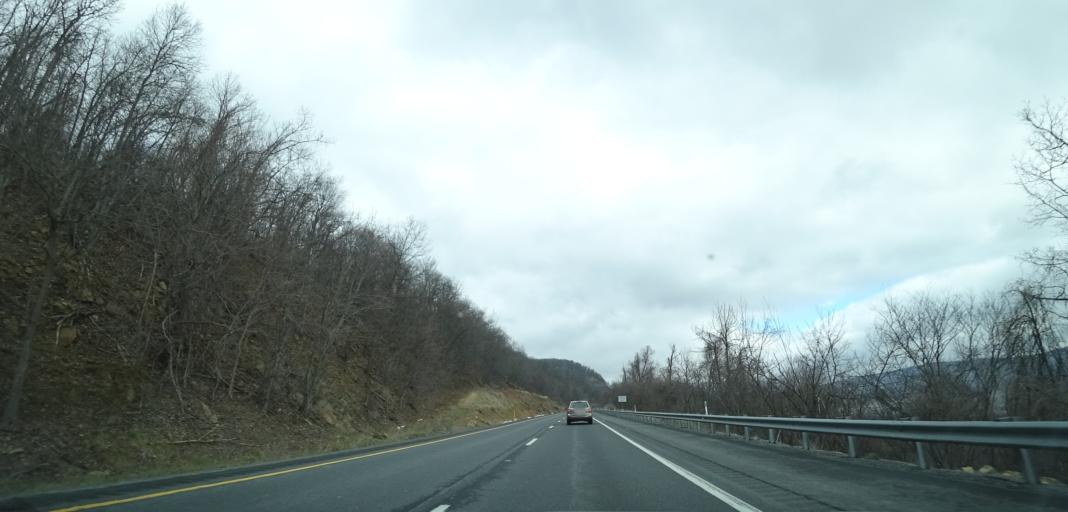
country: US
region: Pennsylvania
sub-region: Bedford County
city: Earlston
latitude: 39.8648
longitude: -78.2616
